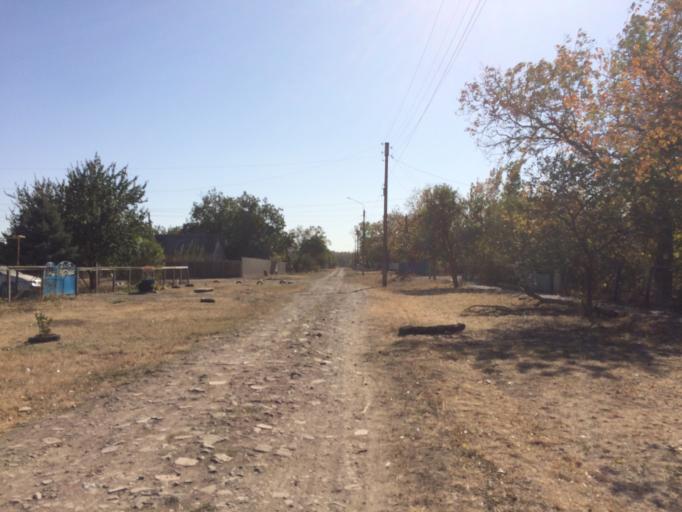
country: RU
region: Rostov
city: Gigant
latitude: 46.5251
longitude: 41.1882
